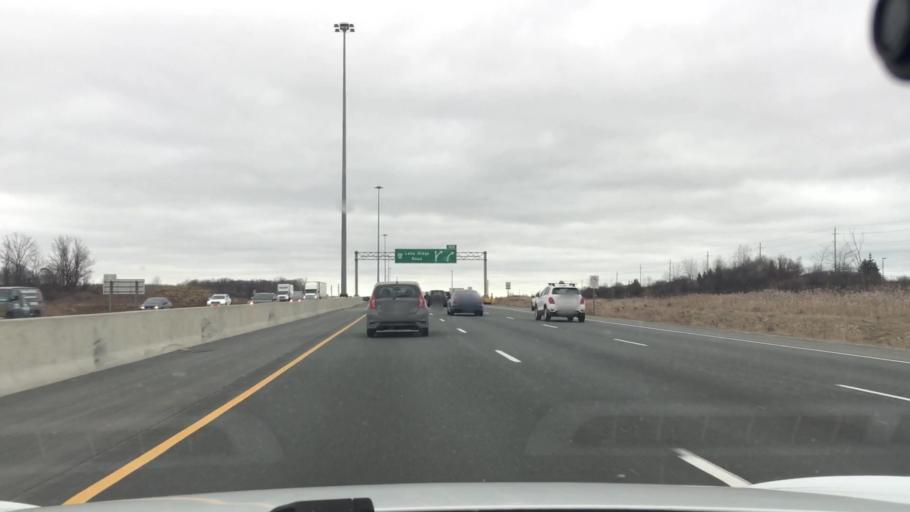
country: CA
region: Ontario
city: Ajax
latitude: 43.8579
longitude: -78.9997
